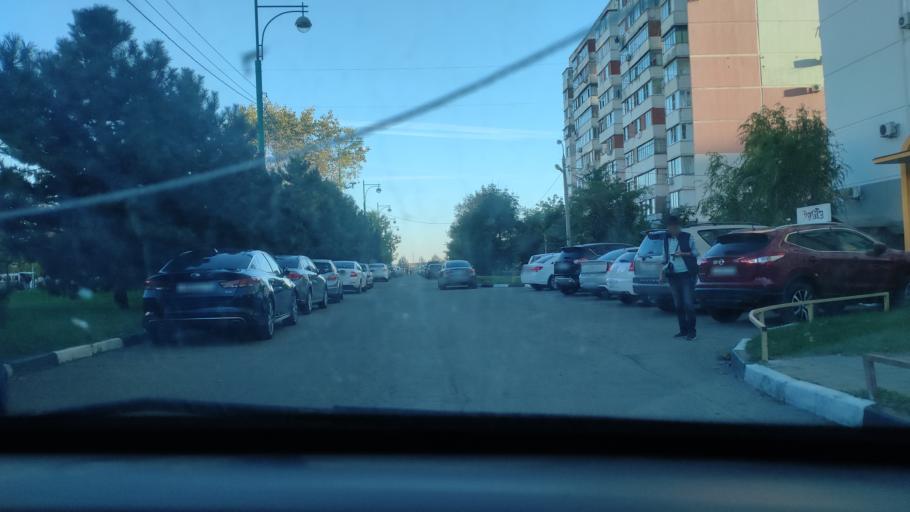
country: RU
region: Adygeya
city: Yablonovskiy
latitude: 45.0286
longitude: 38.9123
